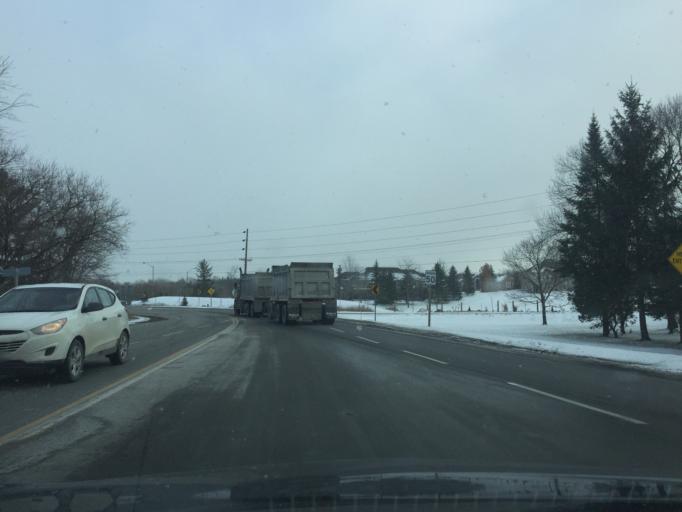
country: CA
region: Ontario
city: Uxbridge
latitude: 44.0338
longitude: -79.2018
